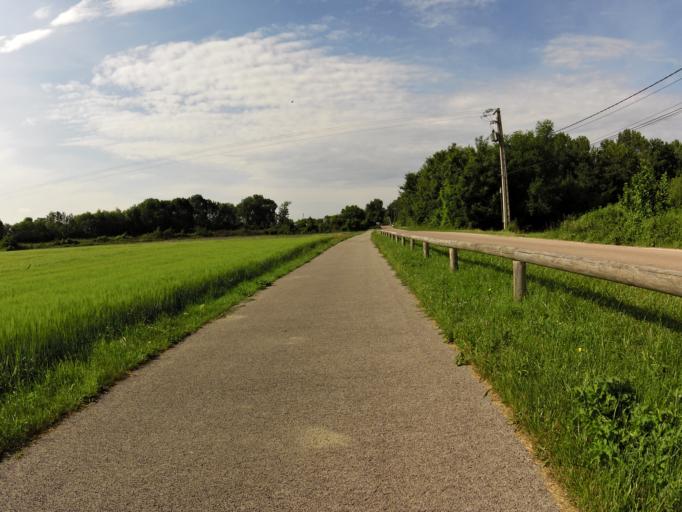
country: FR
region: Champagne-Ardenne
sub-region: Departement de l'Aube
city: Saint-Julien-les-Villas
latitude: 48.2730
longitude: 4.1113
